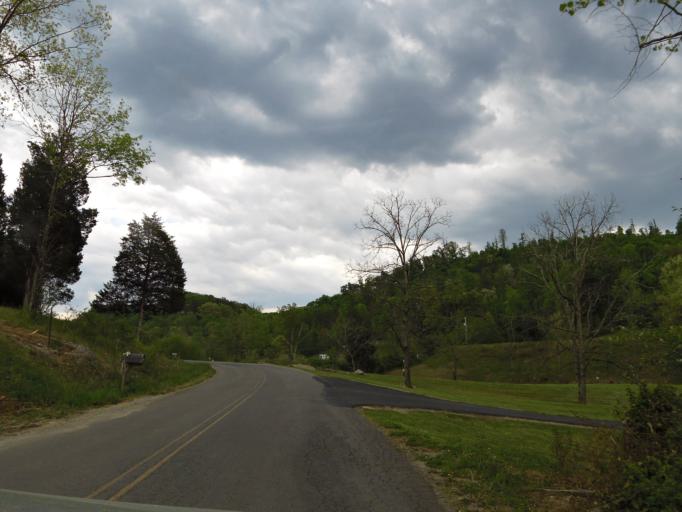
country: US
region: Tennessee
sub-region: Blount County
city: Eagleton Village
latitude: 35.8543
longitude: -83.9213
